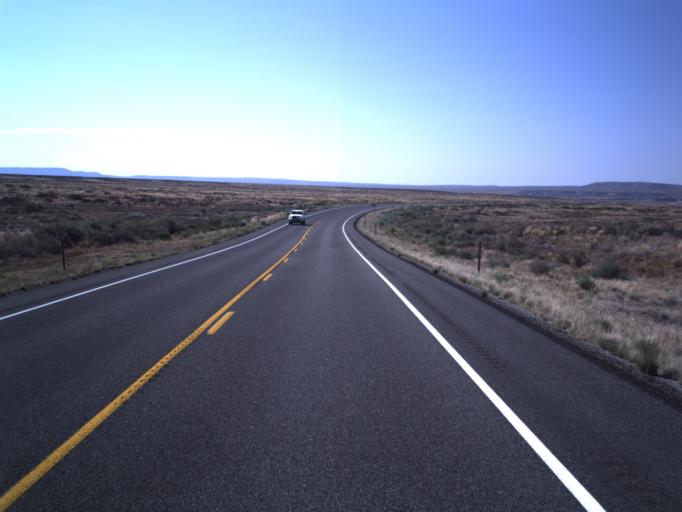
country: US
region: Utah
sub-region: San Juan County
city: Blanding
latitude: 37.3347
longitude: -109.5198
